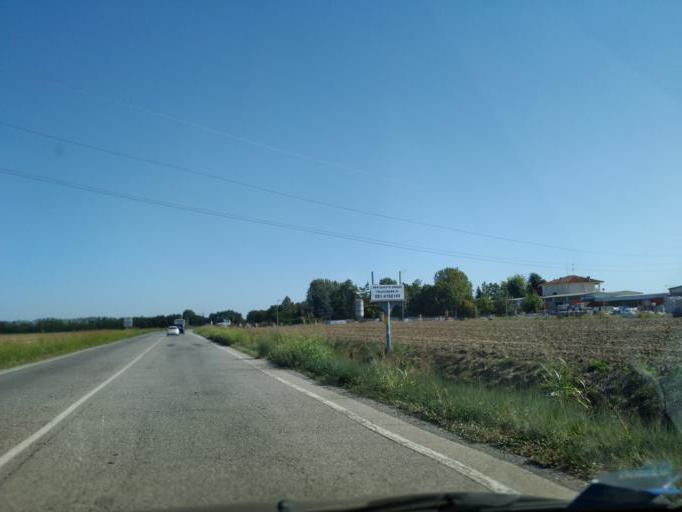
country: IT
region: Emilia-Romagna
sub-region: Provincia di Ferrara
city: Cento
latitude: 44.7438
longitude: 11.2690
